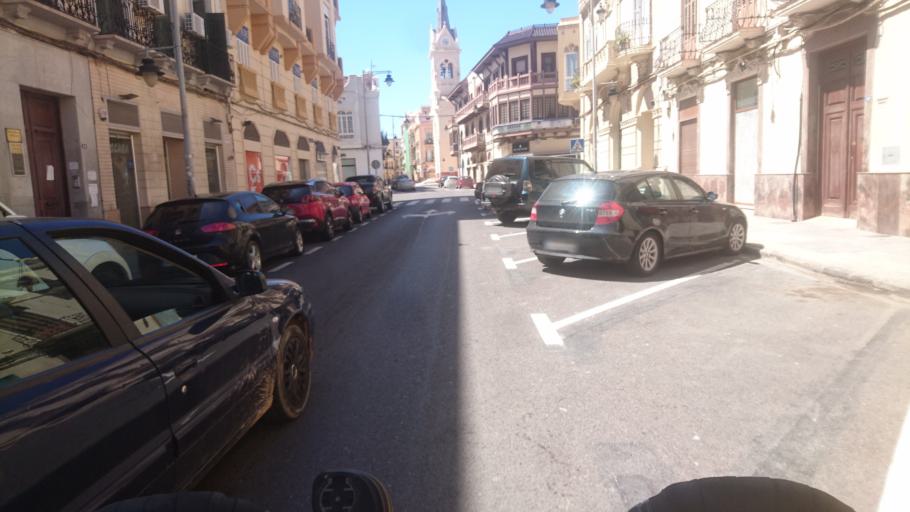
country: ES
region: Melilla
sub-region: Melilla
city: Melilla
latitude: 35.2937
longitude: -2.9393
